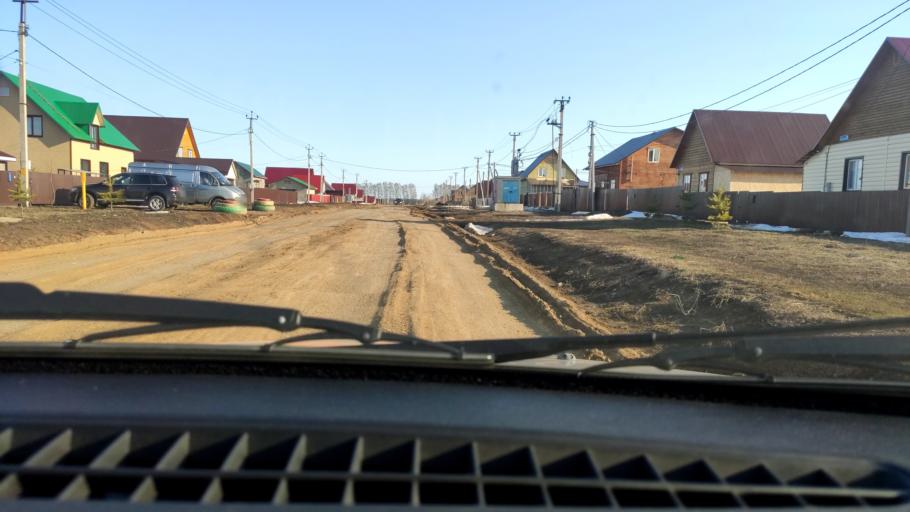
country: RU
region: Bashkortostan
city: Iglino
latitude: 54.8224
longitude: 56.4406
